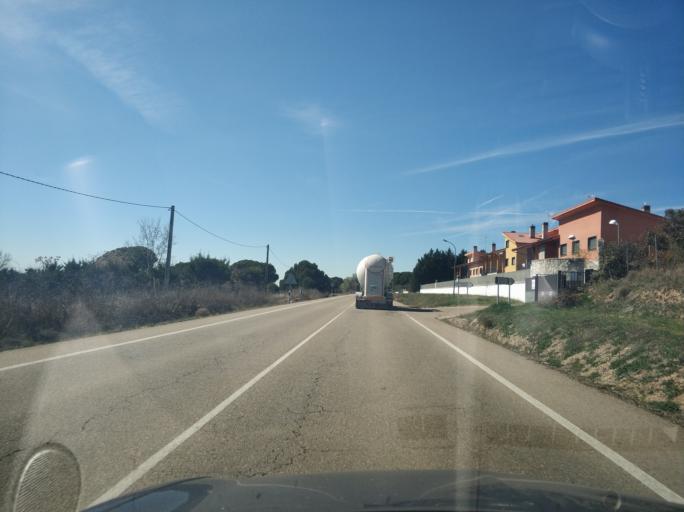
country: ES
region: Castille and Leon
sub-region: Provincia de Valladolid
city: Boecillo
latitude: 41.5463
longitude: -4.6682
